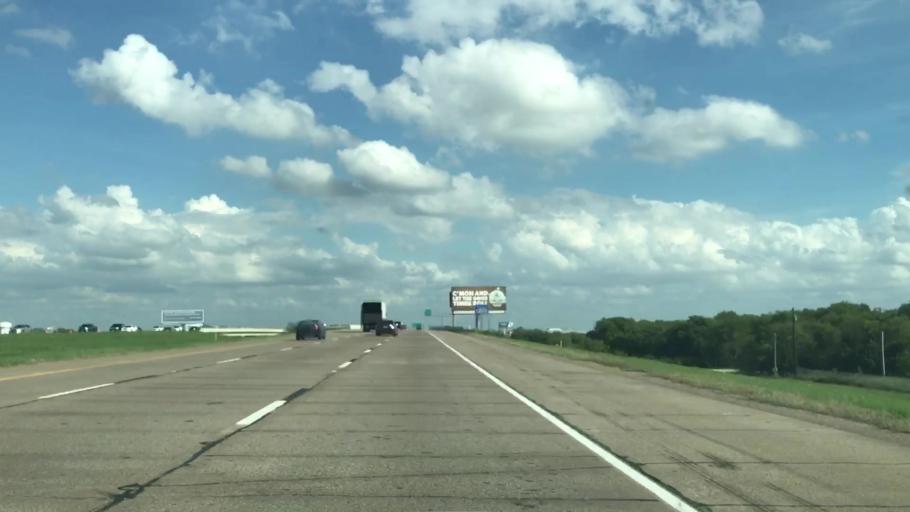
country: US
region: Texas
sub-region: Dallas County
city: Coppell
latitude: 32.9478
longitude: -97.0306
